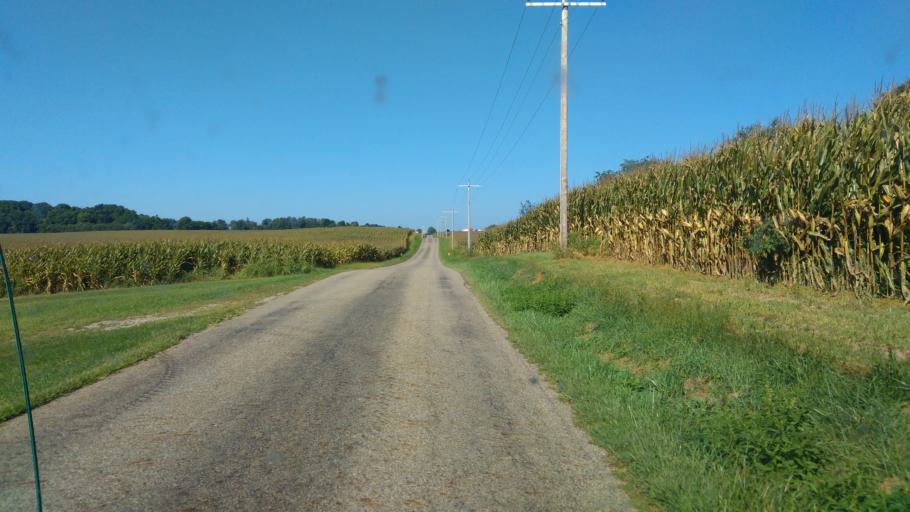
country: US
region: Ohio
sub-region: Knox County
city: Fredericktown
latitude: 40.4595
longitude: -82.4980
